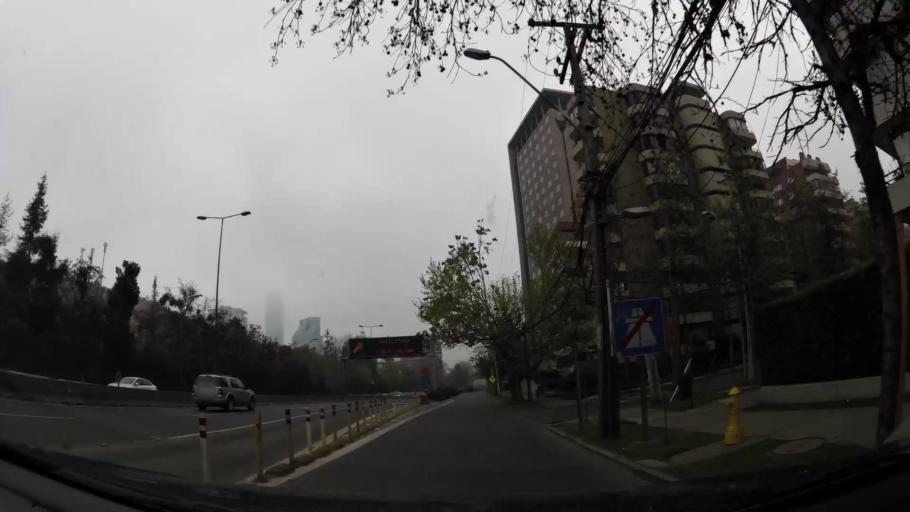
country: CL
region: Santiago Metropolitan
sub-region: Provincia de Santiago
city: Villa Presidente Frei, Nunoa, Santiago, Chile
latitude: -33.4074
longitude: -70.5976
